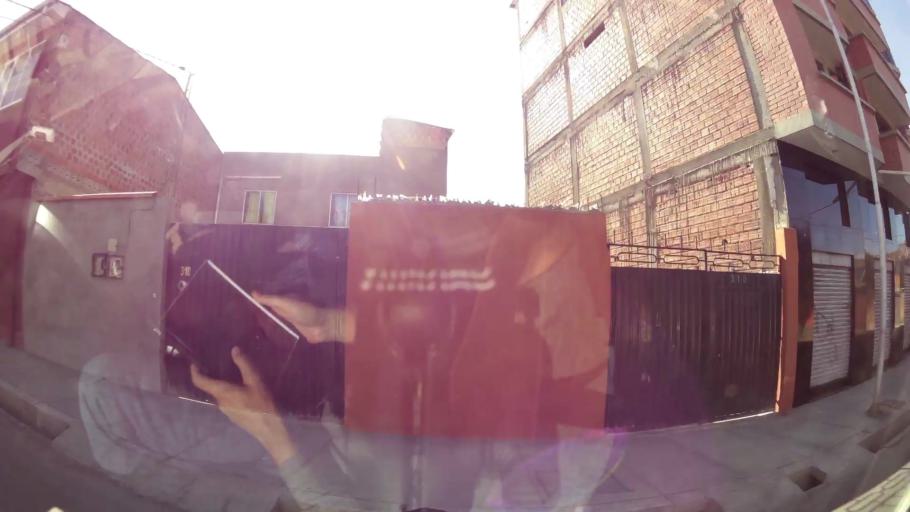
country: BO
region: La Paz
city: La Paz
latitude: -16.5197
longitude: -68.1235
